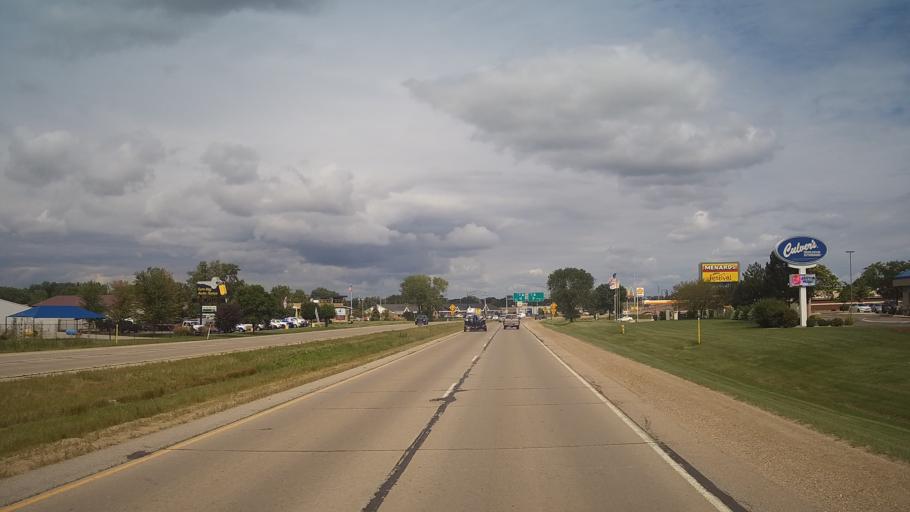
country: US
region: Wisconsin
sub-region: Winnebago County
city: Oshkosh
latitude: 44.0310
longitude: -88.5911
